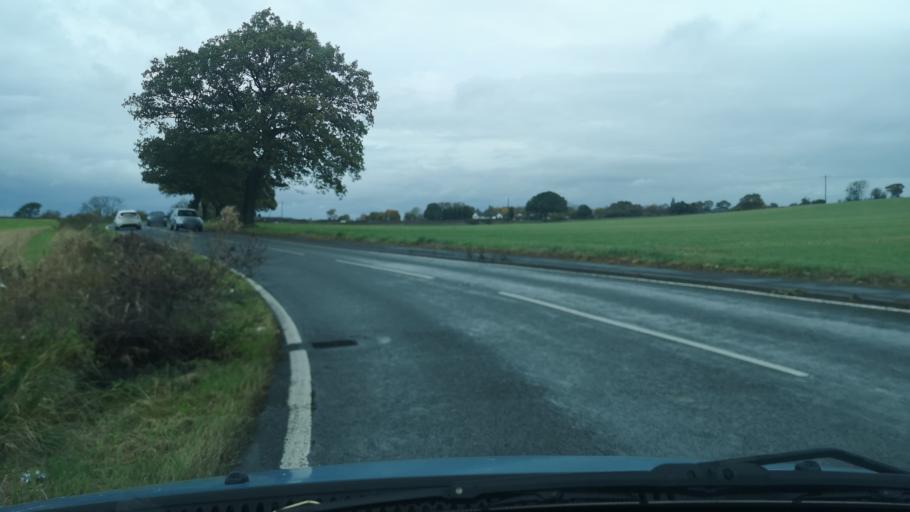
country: GB
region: England
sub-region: City and Borough of Wakefield
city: Featherstone
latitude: 53.6639
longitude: -1.3480
